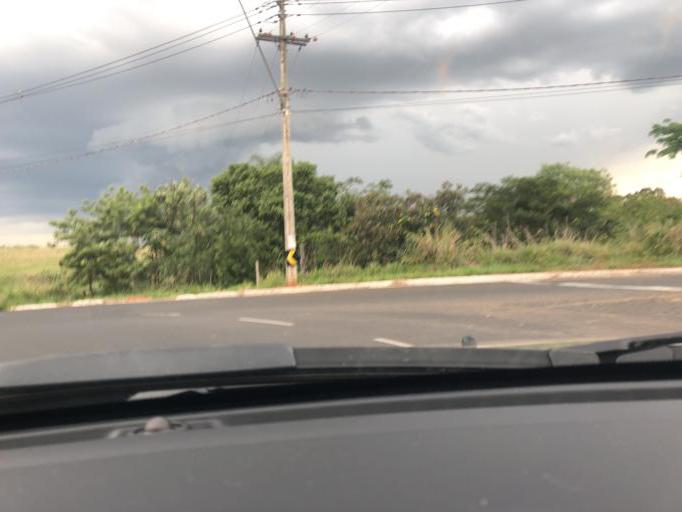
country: BR
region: Sao Paulo
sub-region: Sao Jose Do Rio Preto
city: Sao Jose do Rio Preto
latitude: -20.8305
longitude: -49.4265
